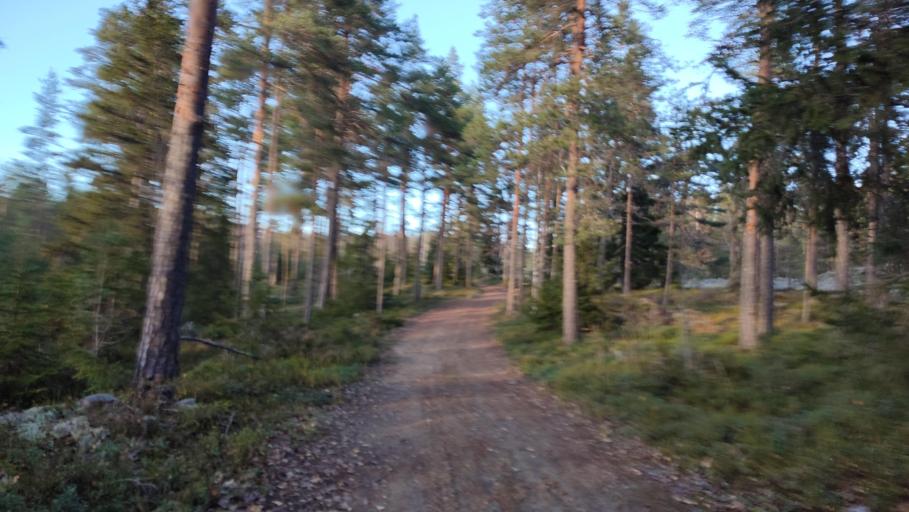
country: FI
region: Southern Ostrobothnia
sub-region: Suupohja
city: Karijoki
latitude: 62.2812
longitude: 21.6436
